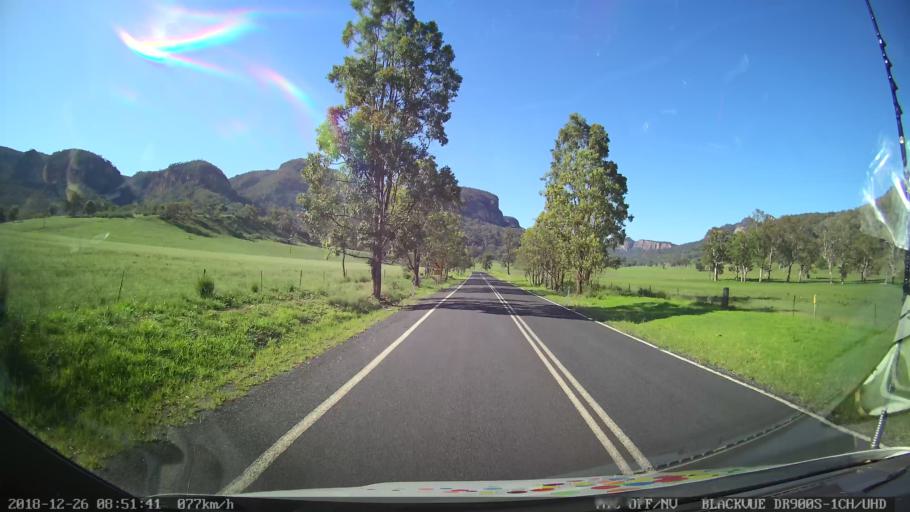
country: AU
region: New South Wales
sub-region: Mid-Western Regional
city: Kandos
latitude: -32.5882
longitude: 150.0882
